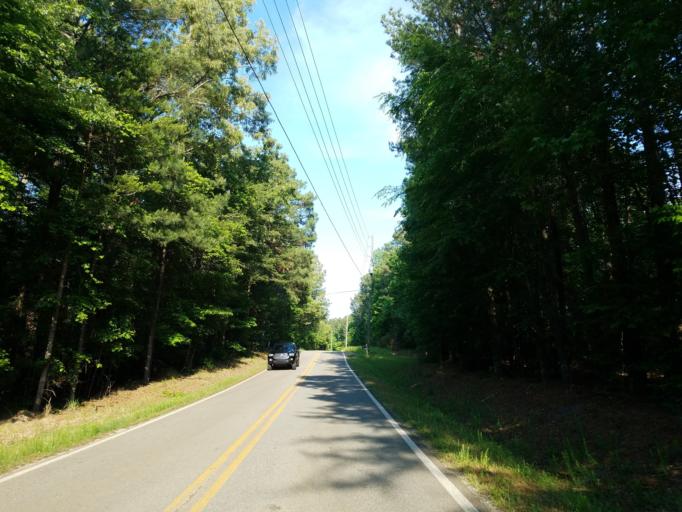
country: US
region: Georgia
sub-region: Pickens County
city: Nelson
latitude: 34.3721
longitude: -84.3319
